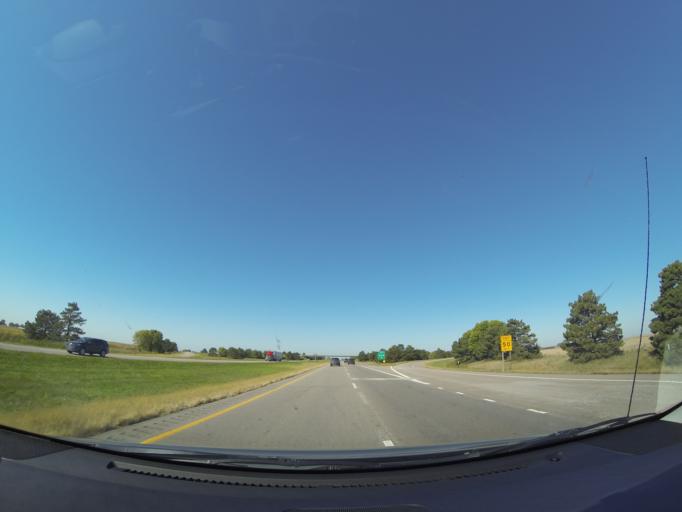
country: US
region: Nebraska
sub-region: Saline County
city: Friend
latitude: 40.8222
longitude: -97.2868
